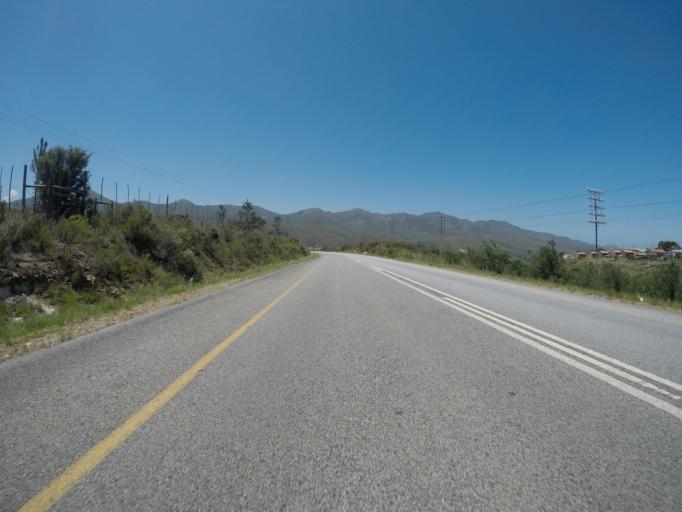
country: ZA
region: Eastern Cape
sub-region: Cacadu District Municipality
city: Kareedouw
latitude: -33.9494
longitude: 24.3025
